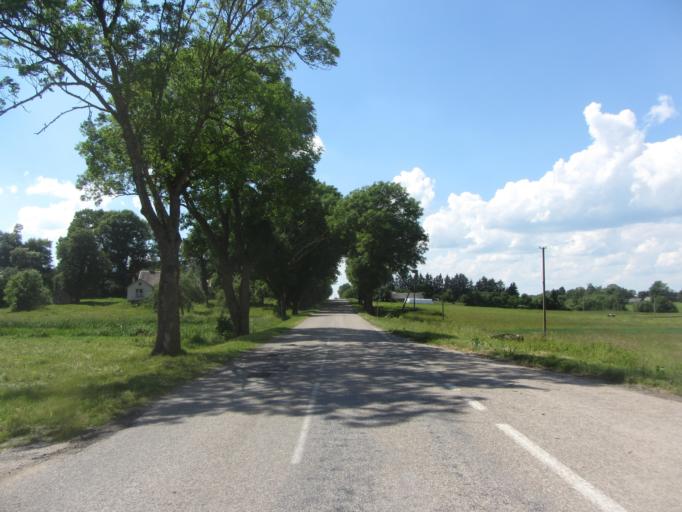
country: LT
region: Alytaus apskritis
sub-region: Alytaus rajonas
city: Daugai
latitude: 54.5058
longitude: 24.3178
